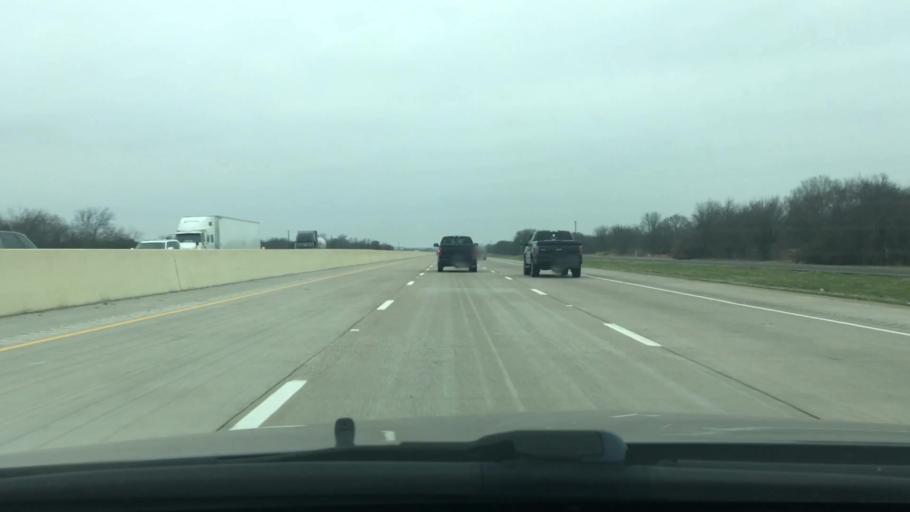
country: US
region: Texas
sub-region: Navarro County
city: Corsicana
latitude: 31.9822
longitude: -96.4239
